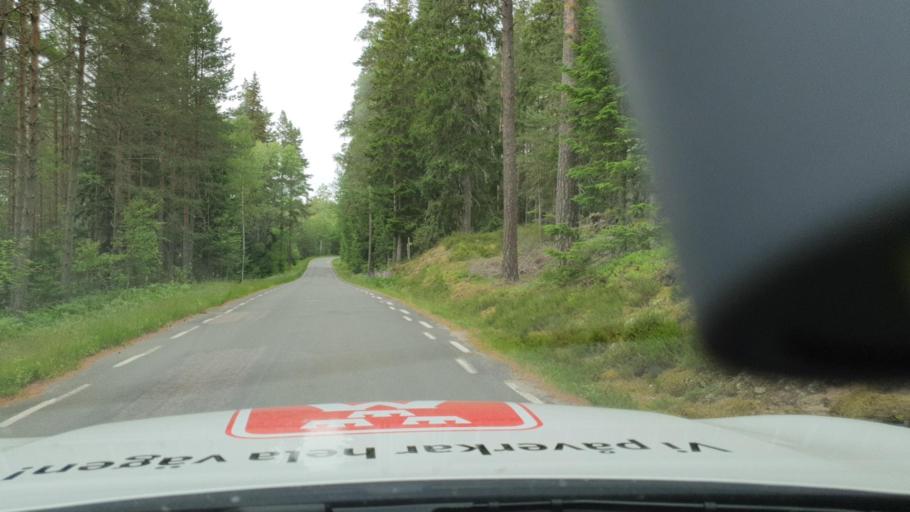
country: SE
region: Vaestra Goetaland
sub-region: Tidaholms Kommun
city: Olofstorp
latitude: 58.1919
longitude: 14.0942
